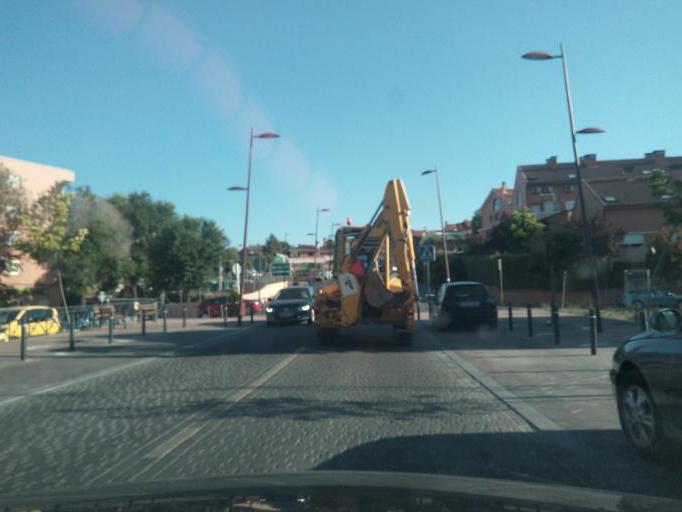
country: ES
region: Madrid
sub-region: Provincia de Madrid
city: Cobena
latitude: 40.5671
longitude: -3.5019
